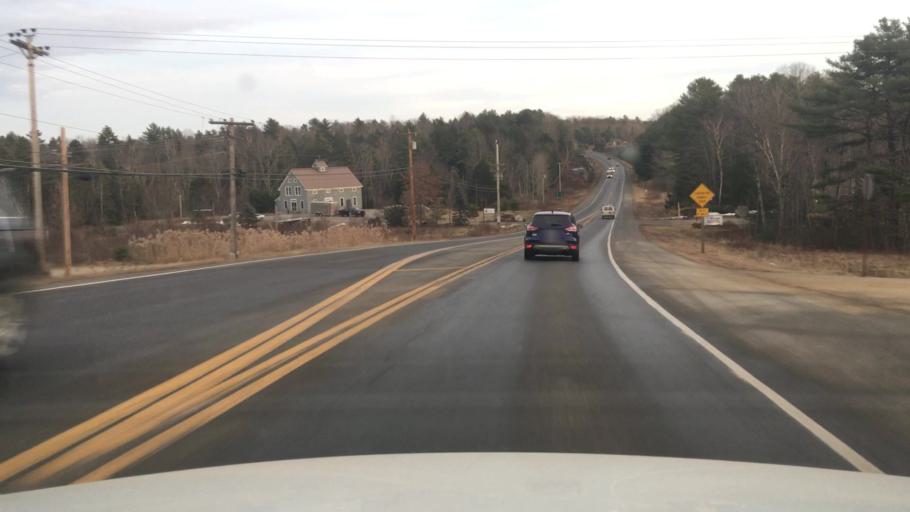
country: US
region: Maine
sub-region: Lincoln County
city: Wiscasset
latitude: 44.0028
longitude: -69.6271
